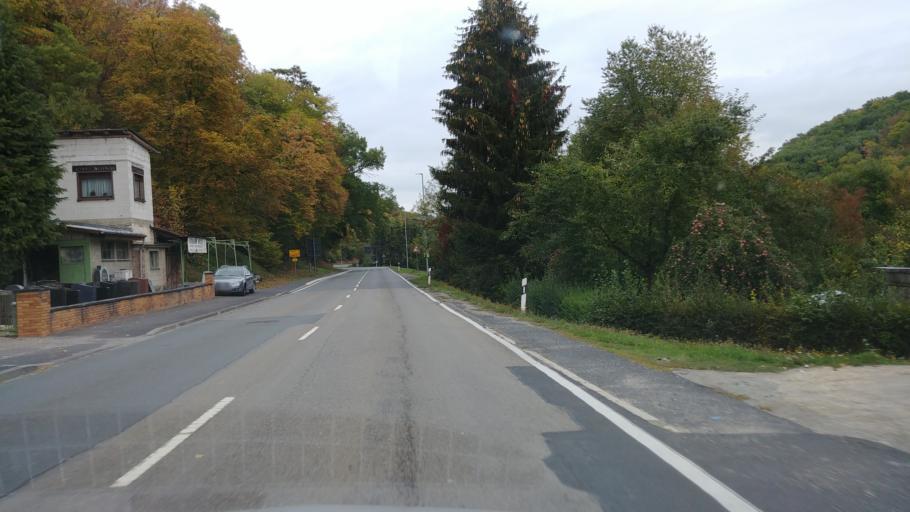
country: DE
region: Rheinland-Pfalz
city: Schiesheim
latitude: 50.2902
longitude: 8.0616
